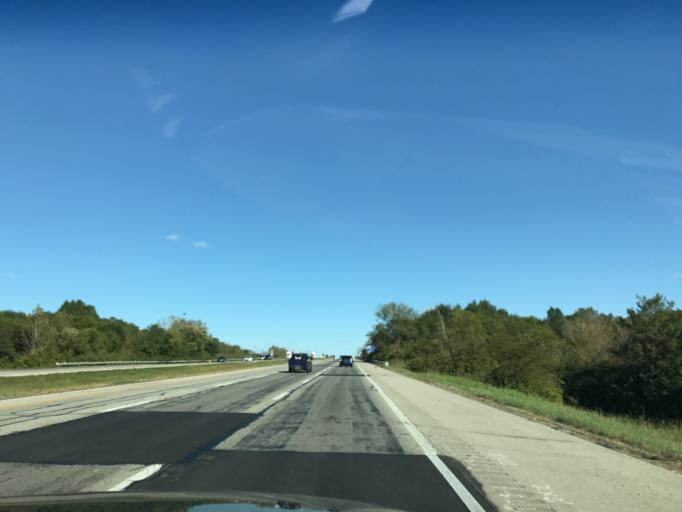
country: US
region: Ohio
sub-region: Franklin County
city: Obetz
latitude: 39.8725
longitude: -82.9661
